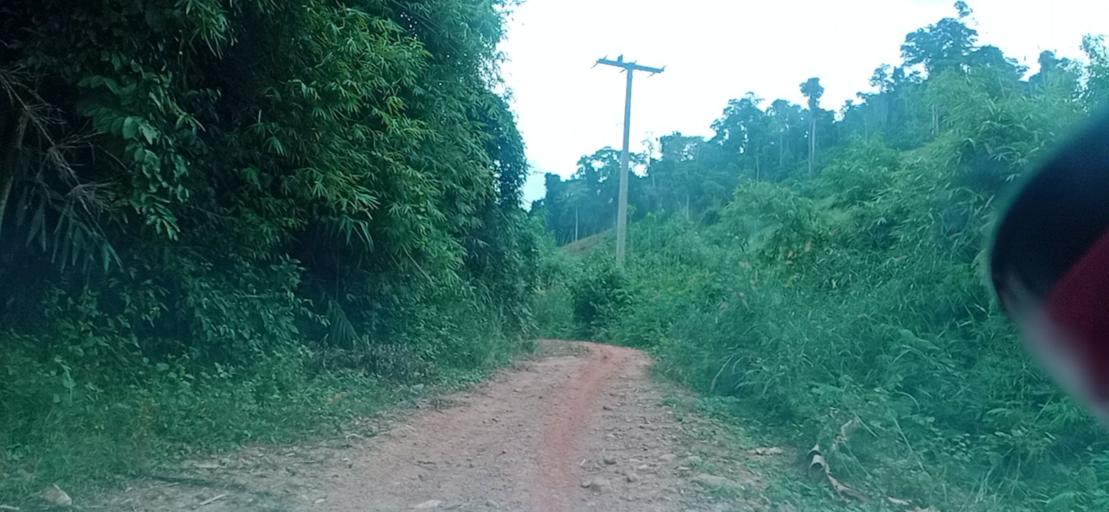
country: TH
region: Changwat Bueng Kan
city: Pak Khat
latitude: 18.5607
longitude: 103.2608
